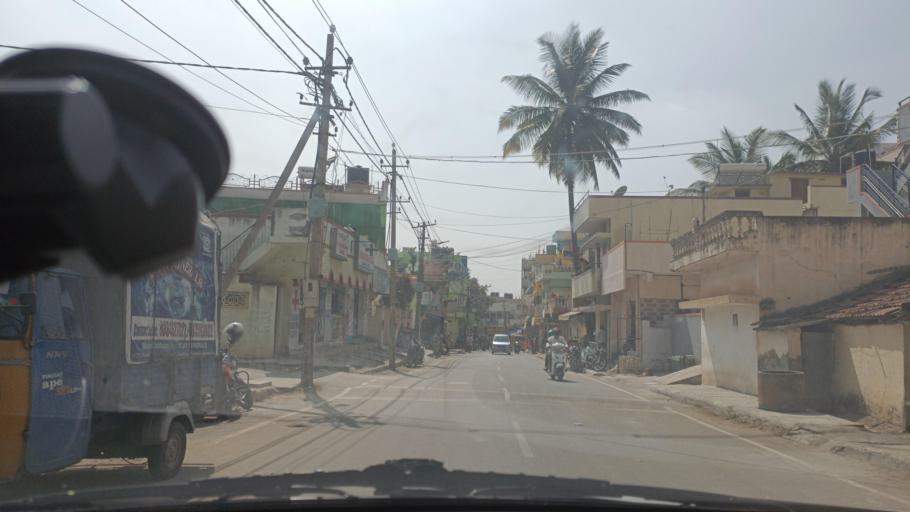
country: IN
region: Karnataka
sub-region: Bangalore Urban
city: Yelahanka
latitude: 13.1063
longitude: 77.6055
